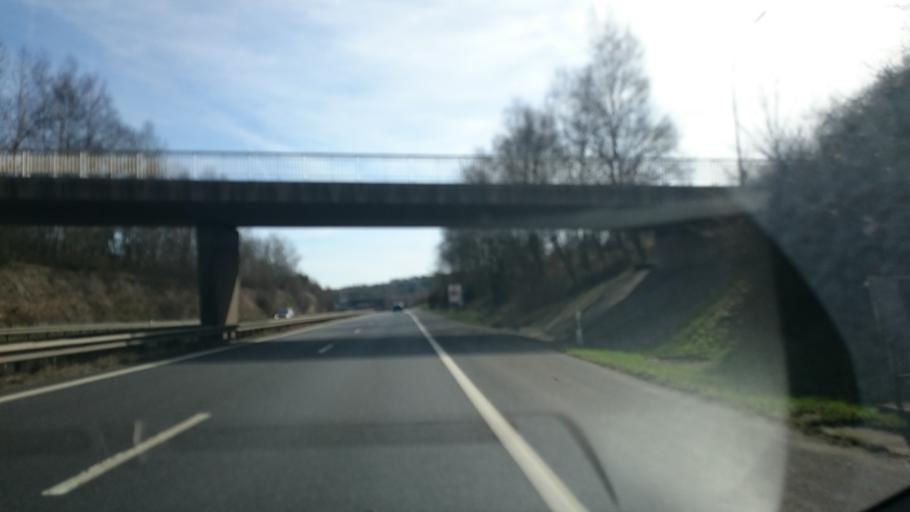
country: LU
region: Luxembourg
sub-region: Canton de Luxembourg
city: Niederanven
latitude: 49.6390
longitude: 6.2327
